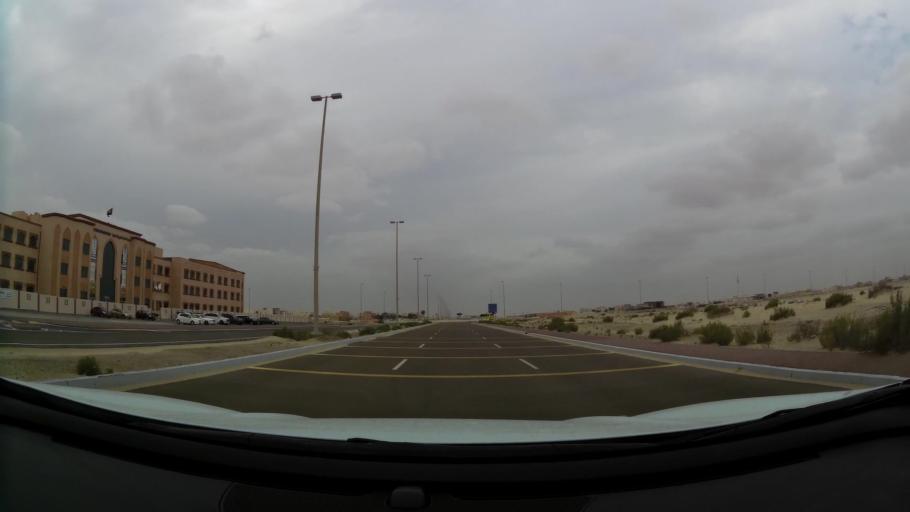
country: AE
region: Abu Dhabi
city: Abu Dhabi
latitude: 24.3614
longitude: 54.6344
